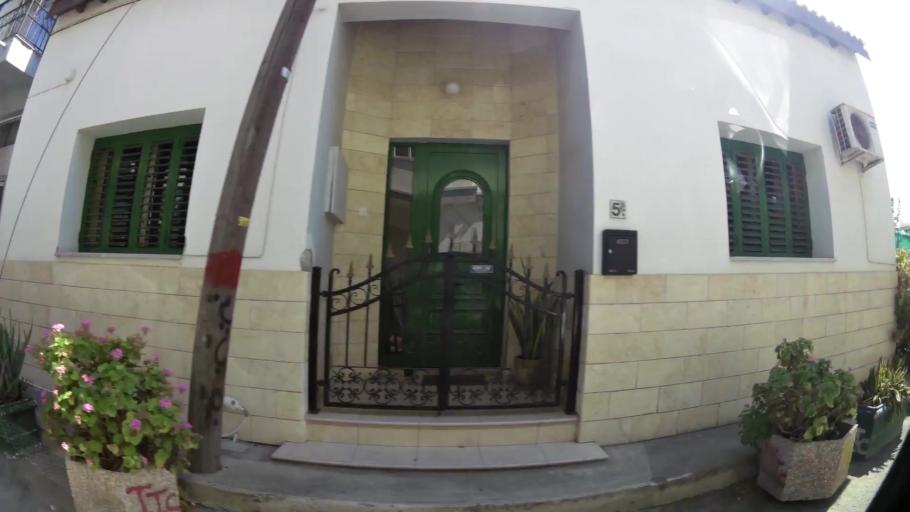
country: CY
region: Larnaka
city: Larnaca
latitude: 34.9109
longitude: 33.6340
